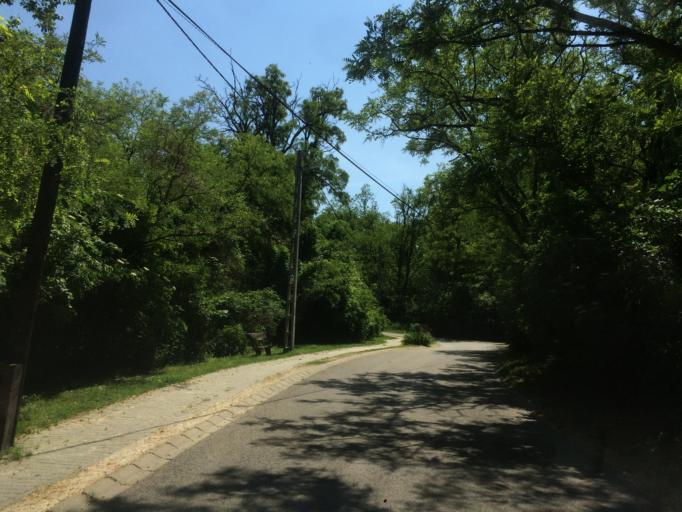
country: HU
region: Pest
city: Pilisszentivan
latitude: 47.6036
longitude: 18.9014
